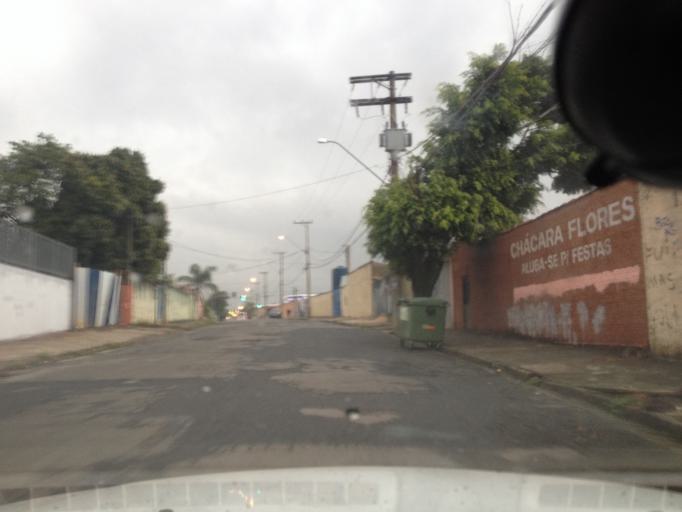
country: BR
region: Sao Paulo
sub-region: Salto
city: Salto
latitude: -23.1914
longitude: -47.2686
